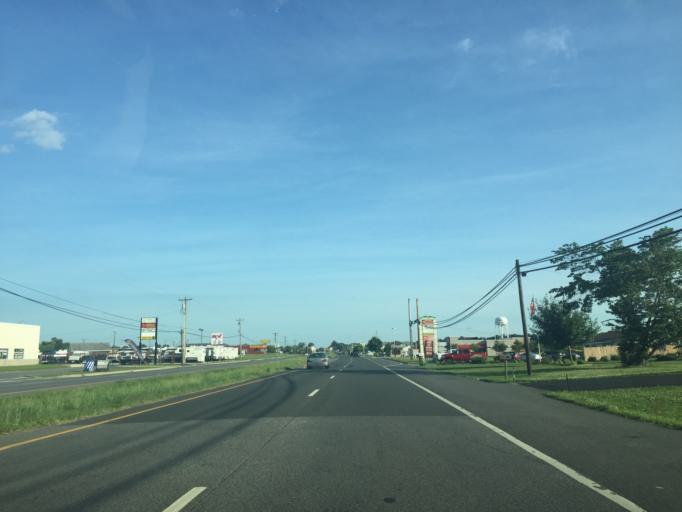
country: US
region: Delaware
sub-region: Kent County
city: Smyrna
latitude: 39.2872
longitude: -75.5950
